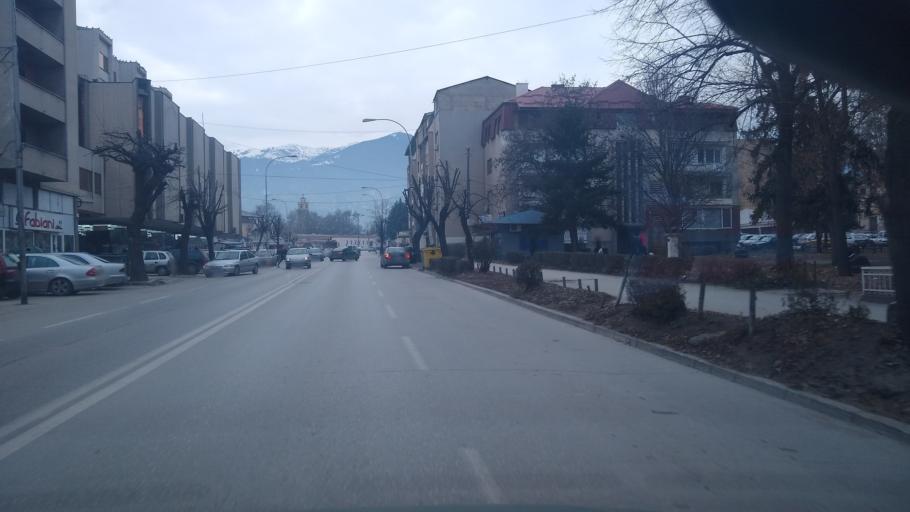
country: MK
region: Bitola
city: Bitola
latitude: 41.0336
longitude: 21.3377
